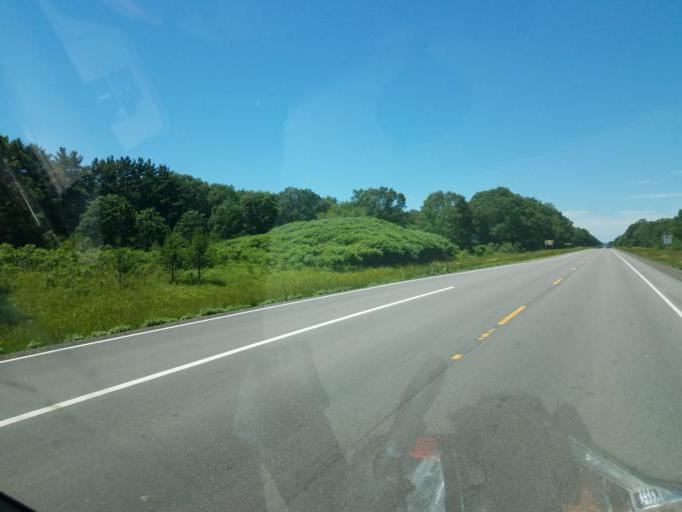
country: US
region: Wisconsin
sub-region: Juneau County
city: New Lisbon
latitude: 44.0257
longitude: -90.2375
